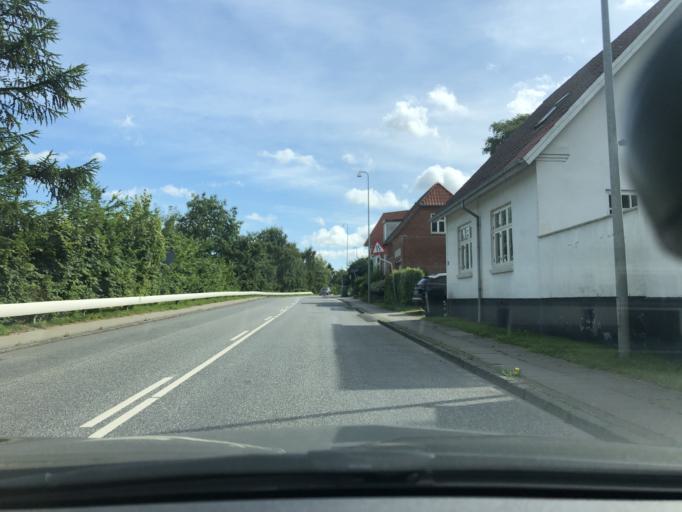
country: DK
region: South Denmark
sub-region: Vejle Kommune
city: Vejle
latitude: 55.7014
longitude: 9.5171
